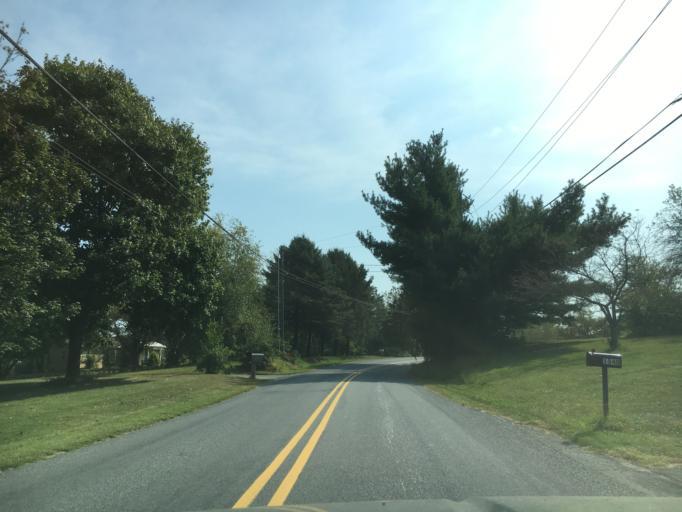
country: US
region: Pennsylvania
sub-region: Berks County
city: Topton
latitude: 40.5729
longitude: -75.7081
